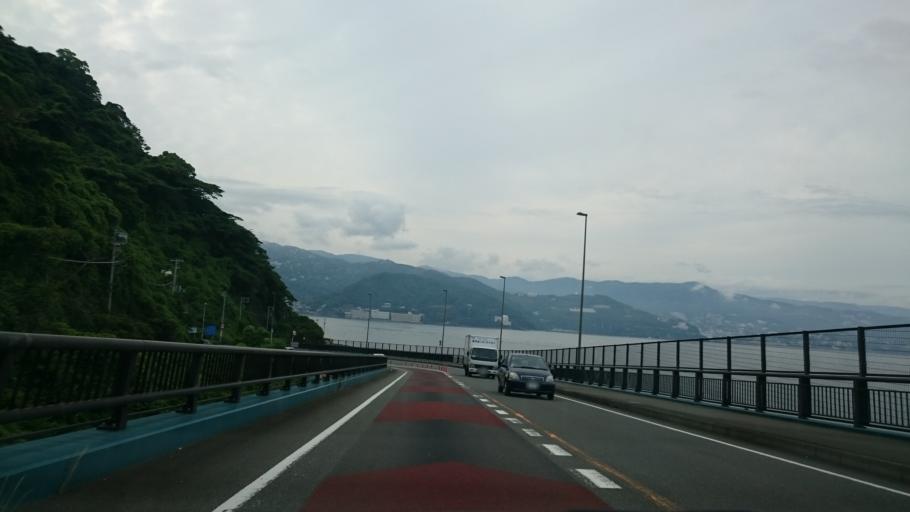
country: JP
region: Shizuoka
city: Atami
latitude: 35.0471
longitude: 139.0977
